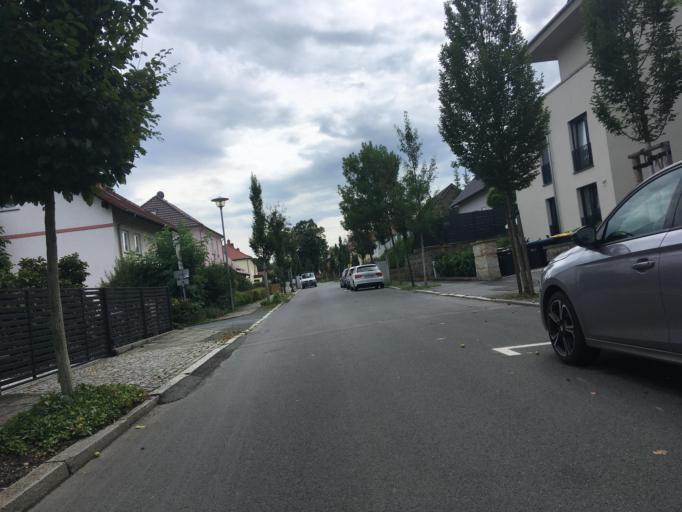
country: DE
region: Saxony
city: Pirna
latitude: 50.9487
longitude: 13.9274
